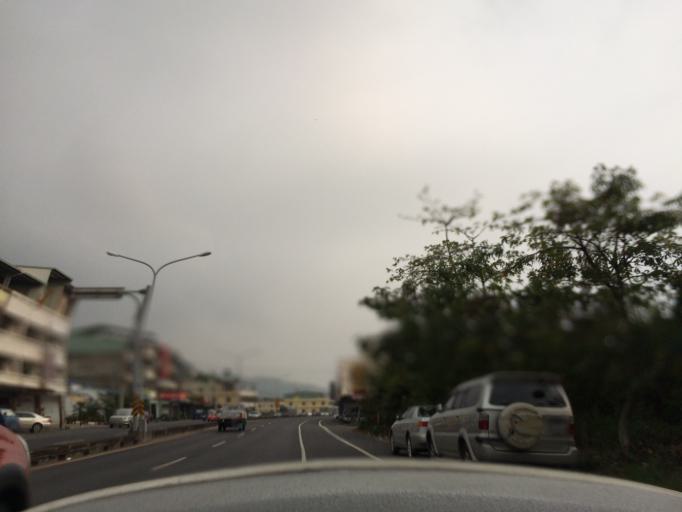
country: TW
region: Taiwan
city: Zhongxing New Village
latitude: 24.0410
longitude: 120.6920
